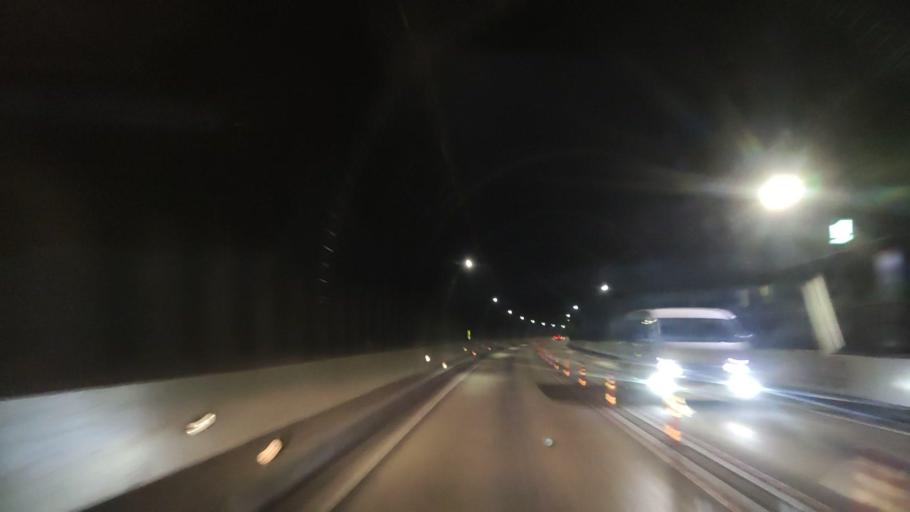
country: JP
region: Hiroshima
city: Innoshima
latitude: 34.1837
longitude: 133.0688
